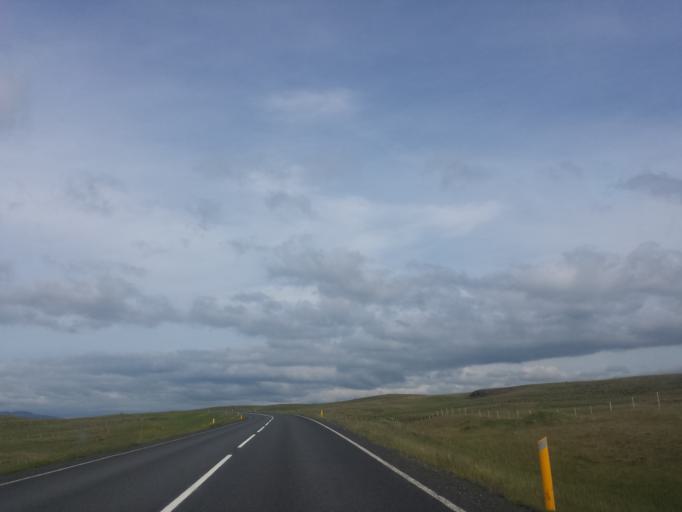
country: IS
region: West
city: Borgarnes
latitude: 65.2782
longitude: -21.0651
